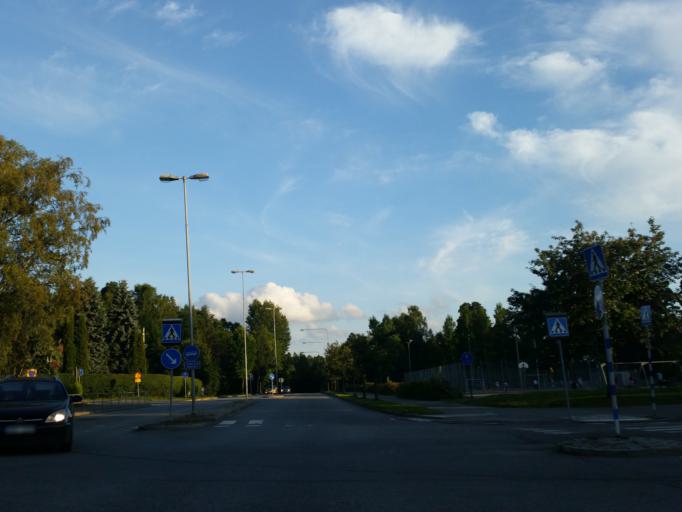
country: SE
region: Stockholm
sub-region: Sodertalje Kommun
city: Soedertaelje
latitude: 59.2059
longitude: 17.6003
